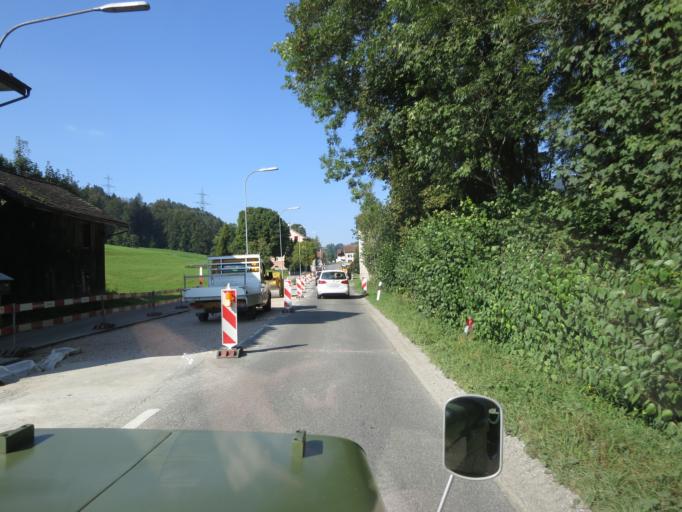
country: CH
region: Zurich
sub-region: Bezirk Hinwil
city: Wald
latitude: 47.2917
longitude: 8.9166
